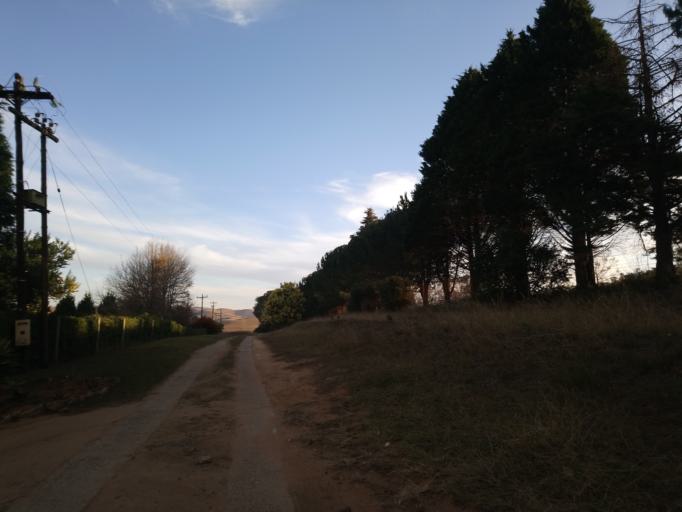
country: ZA
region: KwaZulu-Natal
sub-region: uMgungundlovu District Municipality
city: Mooirivier
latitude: -29.3289
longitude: 29.9203
